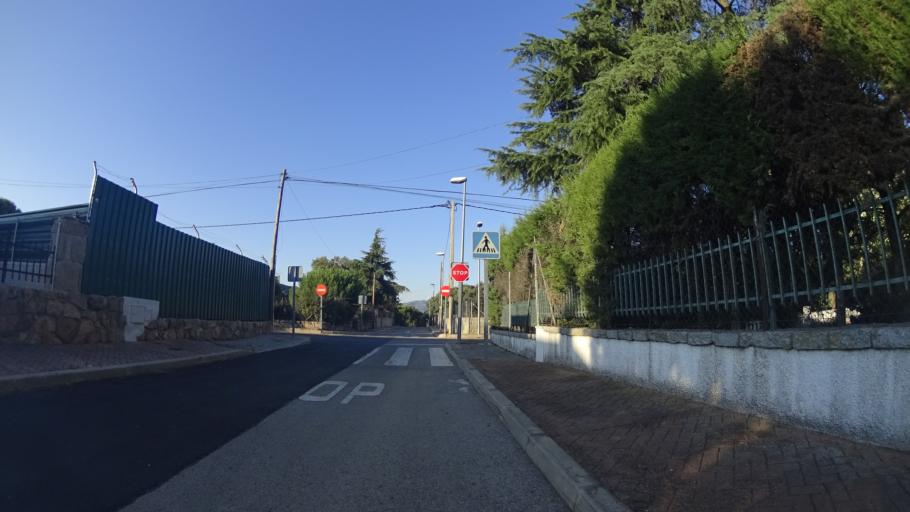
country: ES
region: Madrid
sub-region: Provincia de Madrid
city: Galapagar
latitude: 40.5674
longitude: -4.0034
